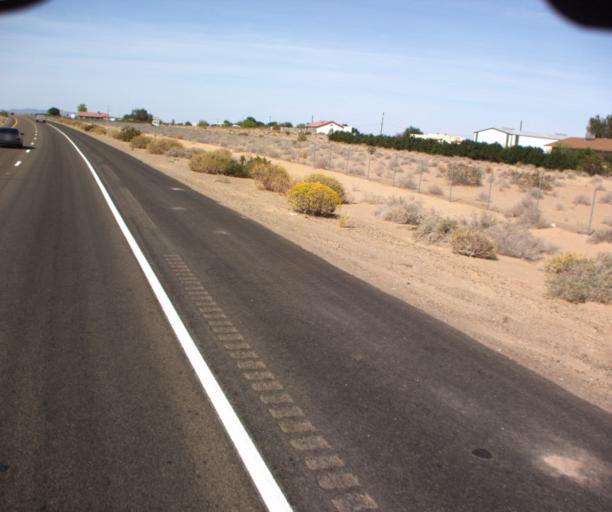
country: US
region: Arizona
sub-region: Yuma County
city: Fortuna Foothills
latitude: 32.6278
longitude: -114.5199
